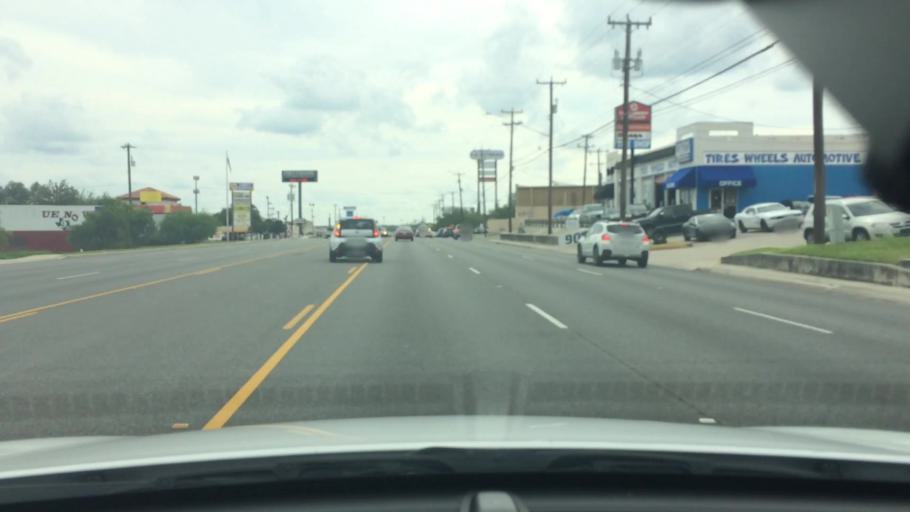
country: US
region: Texas
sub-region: Bexar County
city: Leon Valley
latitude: 29.5264
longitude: -98.5972
